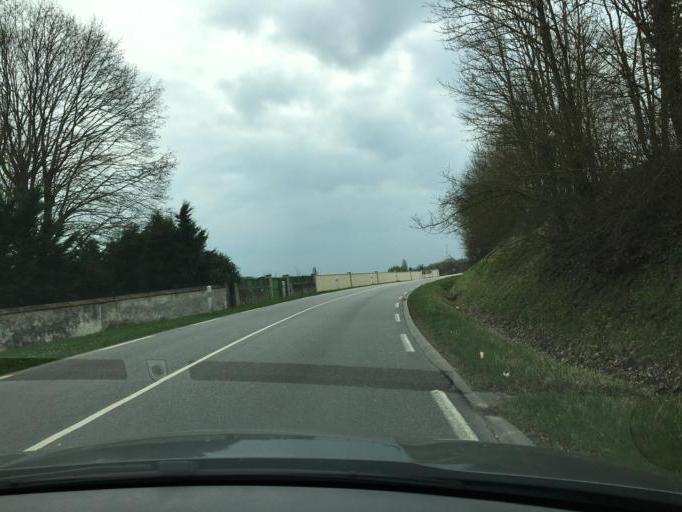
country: FR
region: Ile-de-France
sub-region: Departement des Yvelines
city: Mantes-la-Ville
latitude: 48.9550
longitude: 1.7068
